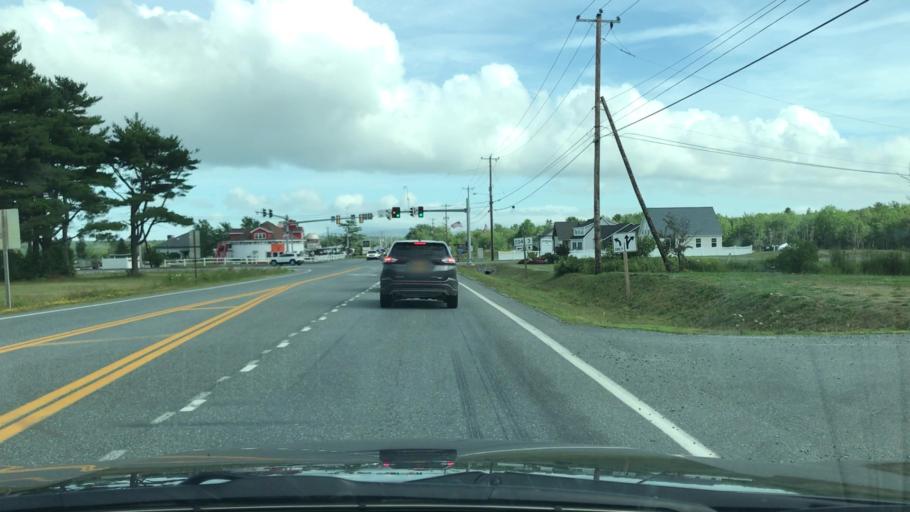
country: US
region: Maine
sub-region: Hancock County
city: Trenton
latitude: 44.4892
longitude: -68.3717
